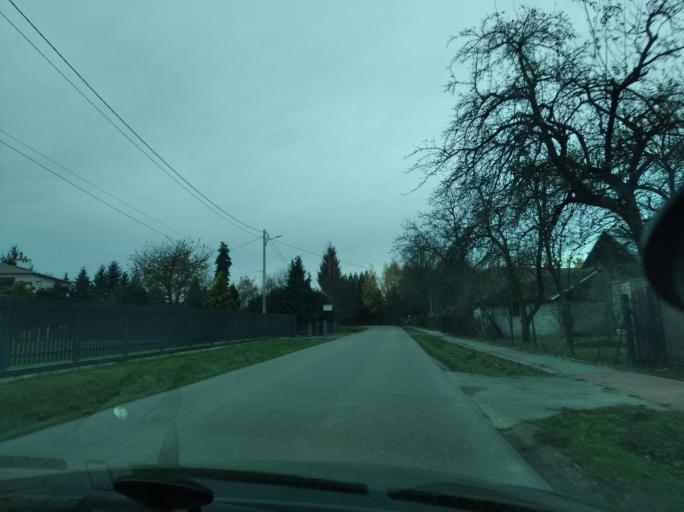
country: PL
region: Subcarpathian Voivodeship
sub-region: Powiat lancucki
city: Lancut
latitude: 50.0960
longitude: 22.2212
